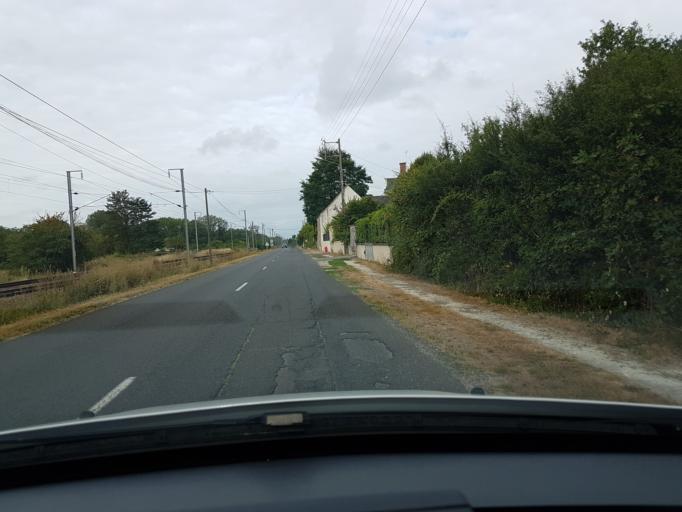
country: FR
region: Centre
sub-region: Departement d'Indre-et-Loire
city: Saint-Martin-le-Beau
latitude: 47.3510
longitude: 0.9277
